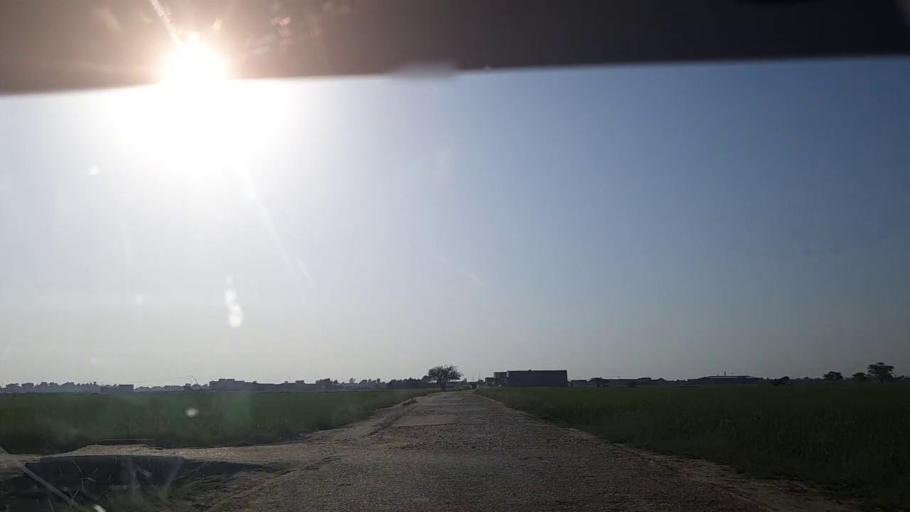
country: PK
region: Sindh
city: Tangwani
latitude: 28.2606
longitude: 69.0100
